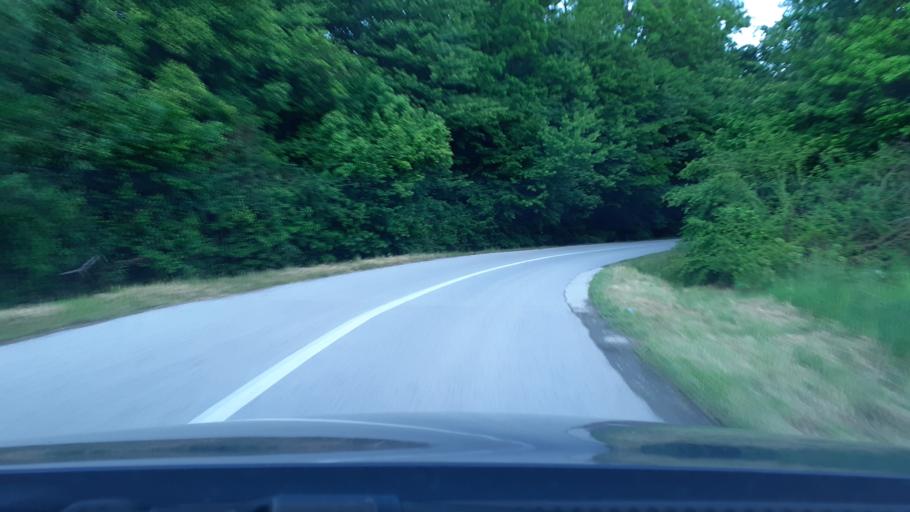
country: HR
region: Pozesko-Slavonska
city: Jaksic
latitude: 45.3488
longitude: 17.7857
